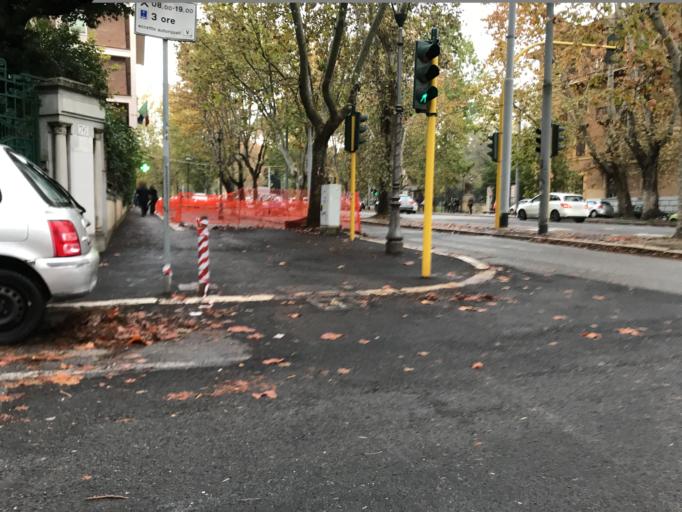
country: IT
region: Latium
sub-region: Citta metropolitana di Roma Capitale
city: Rome
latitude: 41.9166
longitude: 12.5124
